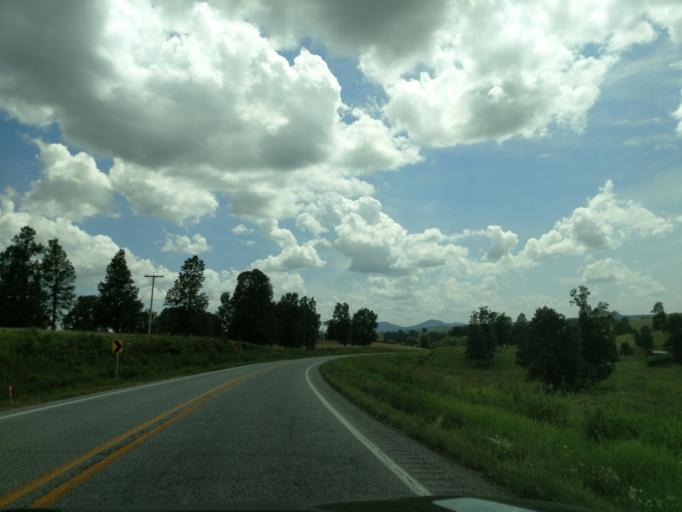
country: US
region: Arkansas
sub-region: Boone County
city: Harrison
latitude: 36.2042
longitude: -92.9344
